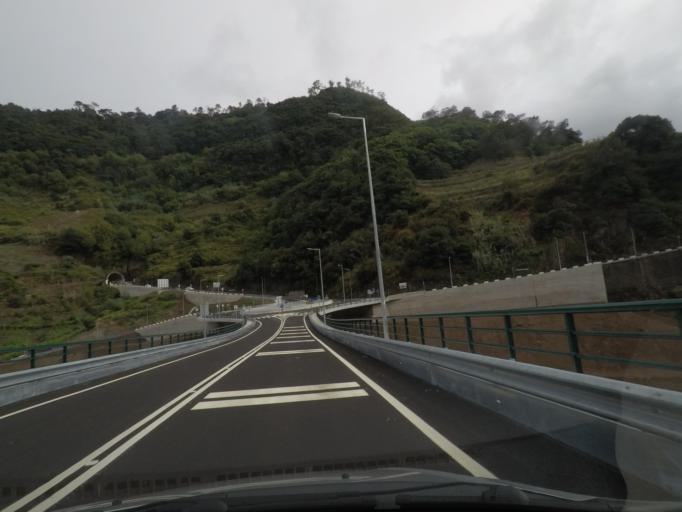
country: PT
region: Madeira
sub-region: Santana
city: Santana
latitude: 32.8158
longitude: -16.9016
